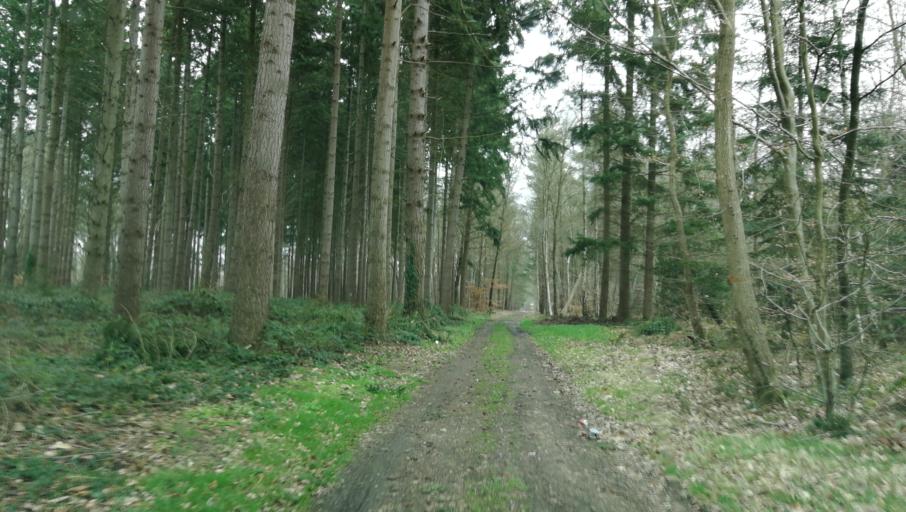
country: FR
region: Haute-Normandie
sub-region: Departement de l'Eure
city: Brionne
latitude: 49.1841
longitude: 0.6978
